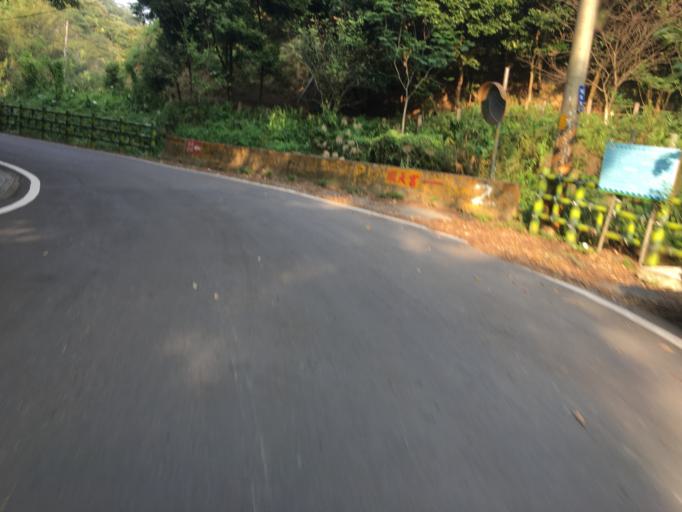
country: TW
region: Taiwan
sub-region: Hsinchu
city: Hsinchu
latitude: 24.7069
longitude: 121.0553
